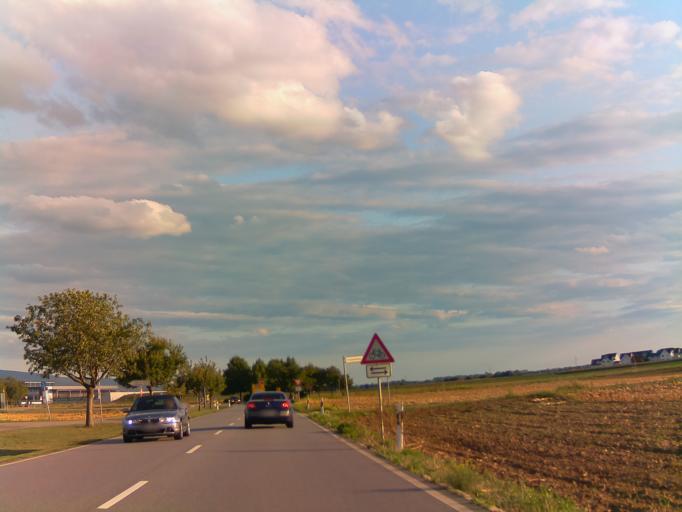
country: DE
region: Baden-Wuerttemberg
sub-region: Karlsruhe Region
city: Heddesheim
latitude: 49.5094
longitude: 8.6178
